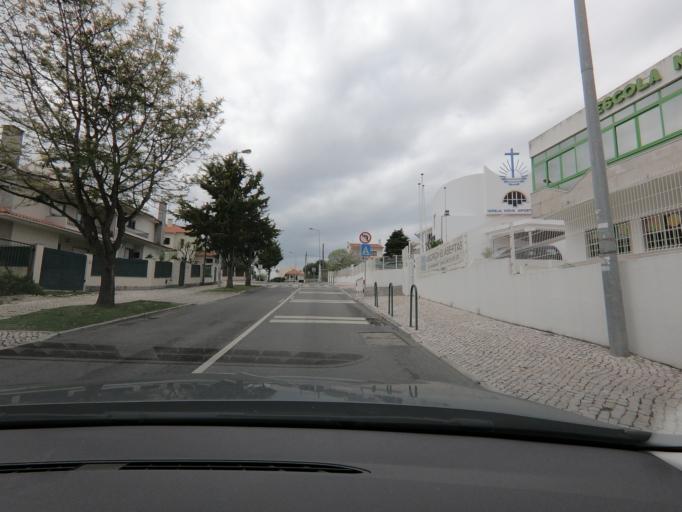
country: PT
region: Lisbon
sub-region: Cascais
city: Sao Domingos de Rana
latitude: 38.7001
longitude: -9.3373
